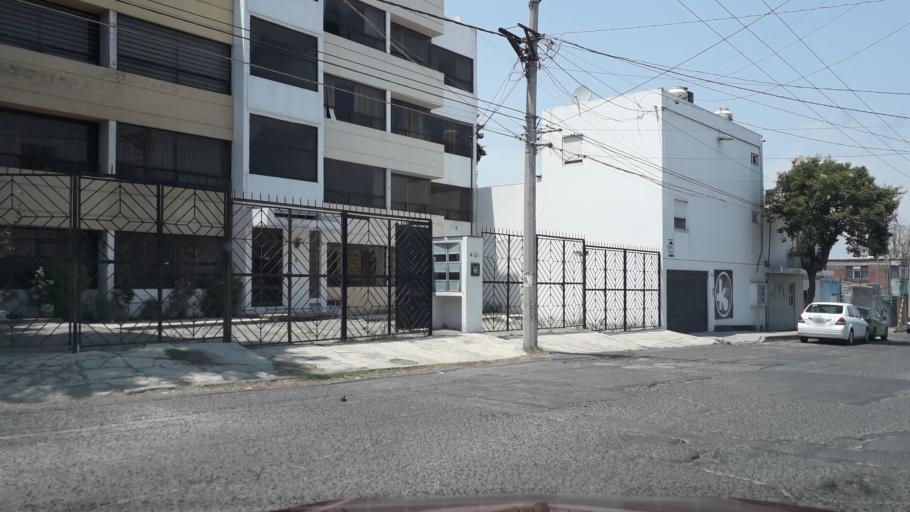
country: MX
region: Puebla
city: Puebla
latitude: 19.0529
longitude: -98.2327
